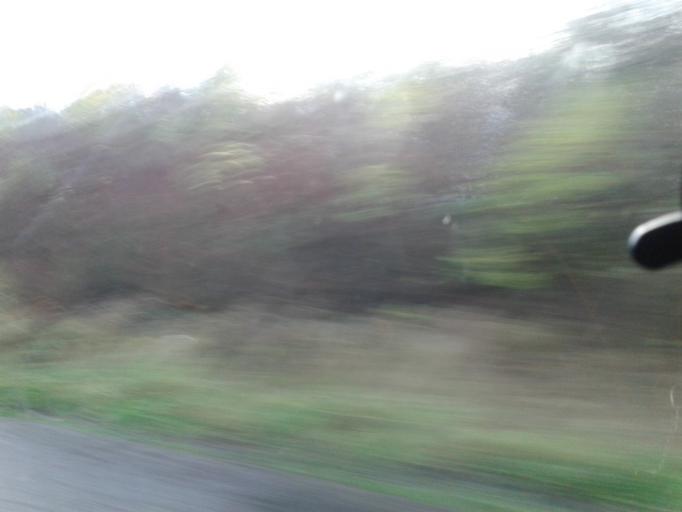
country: IE
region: Leinster
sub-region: Lu
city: Ardee
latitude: 53.9006
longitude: -6.5956
